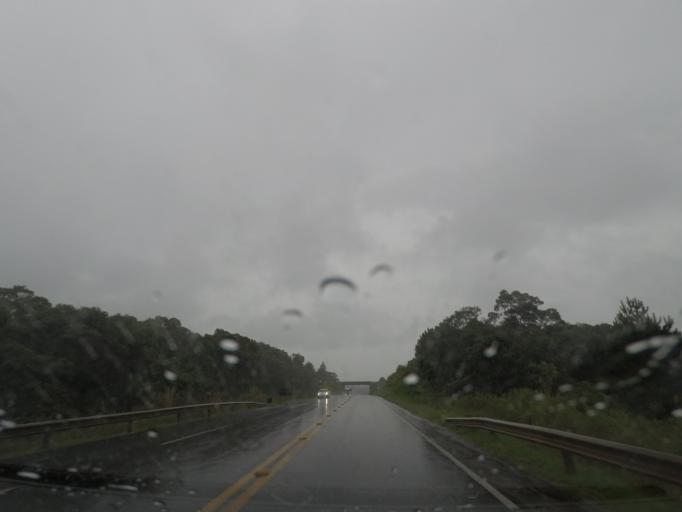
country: BR
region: Parana
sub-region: Almirante Tamandare
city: Almirante Tamandare
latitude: -25.3603
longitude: -49.3136
